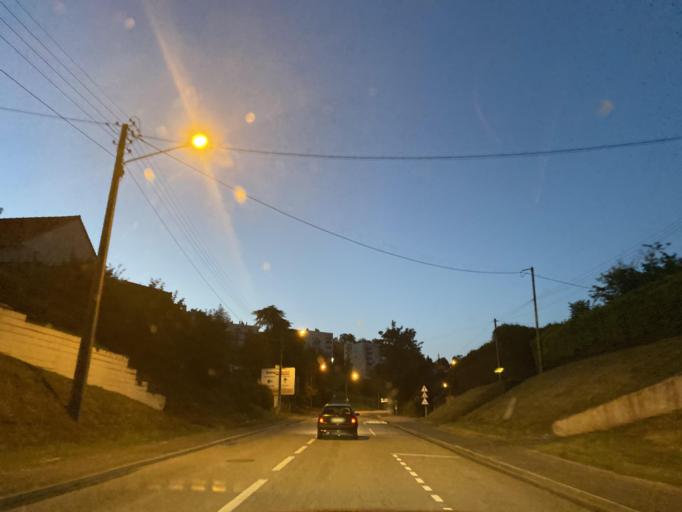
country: FR
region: Haute-Normandie
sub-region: Departement de l'Eure
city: Evreux
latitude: 49.0296
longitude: 1.1643
